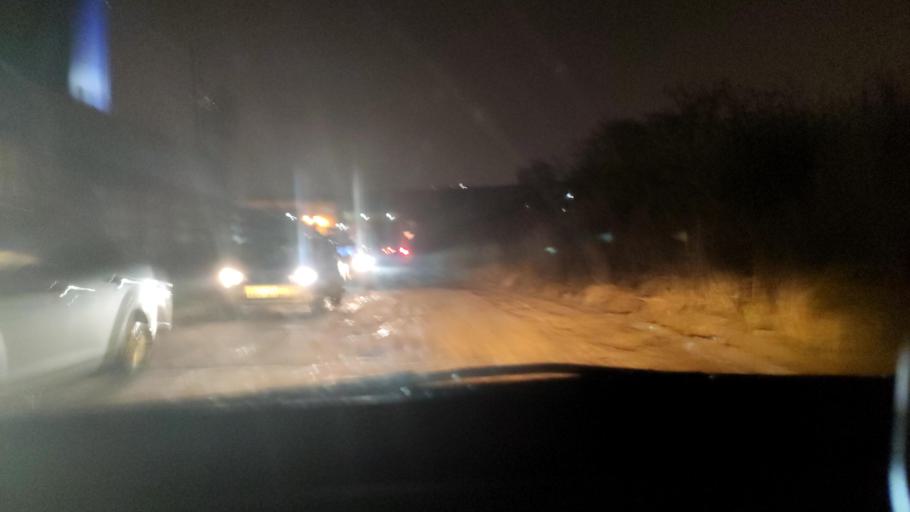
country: RU
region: Voronezj
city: Pridonskoy
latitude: 51.6381
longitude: 39.1102
